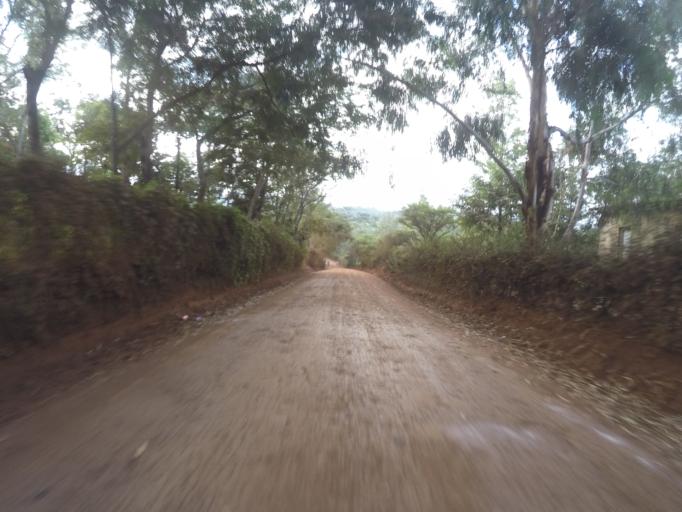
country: TZ
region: Arusha
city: Kiratu
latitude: -3.3333
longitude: 35.6666
